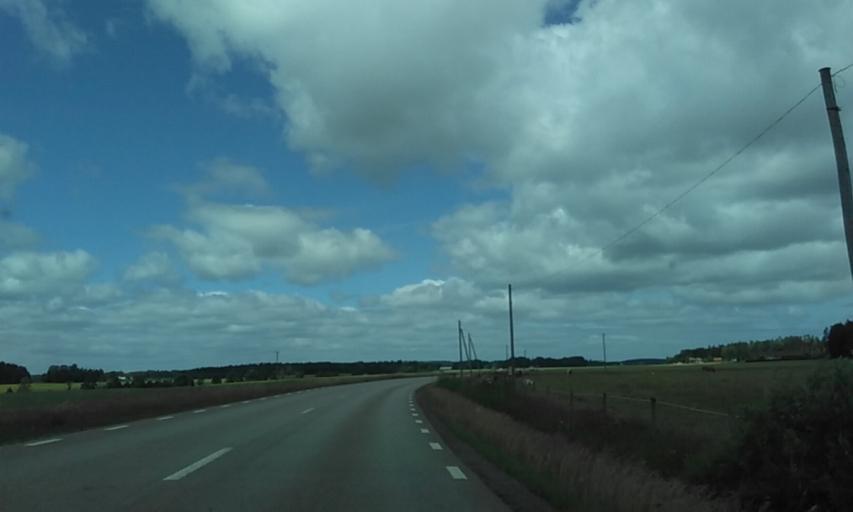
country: SE
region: Vaestra Goetaland
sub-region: Grastorps Kommun
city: Graestorp
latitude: 58.2783
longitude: 12.6760
